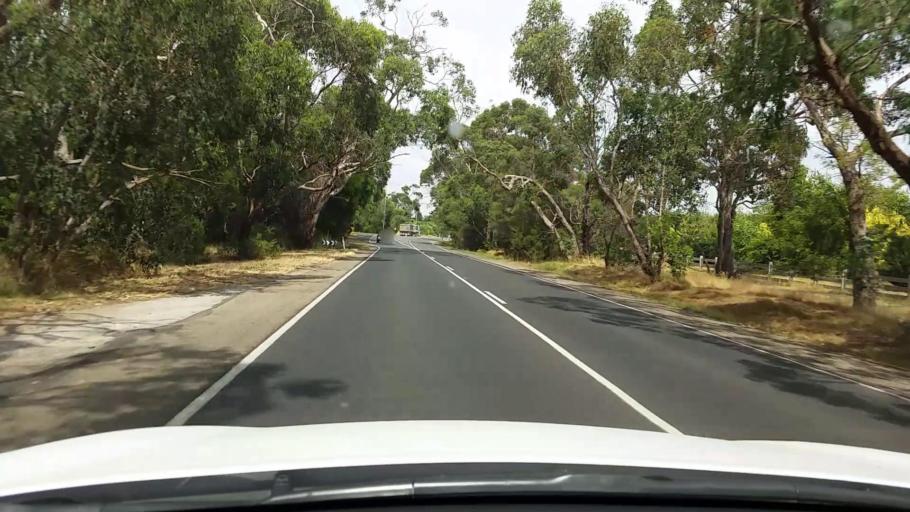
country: AU
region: Victoria
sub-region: Mornington Peninsula
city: Balnarring
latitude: -38.3522
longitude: 145.1575
